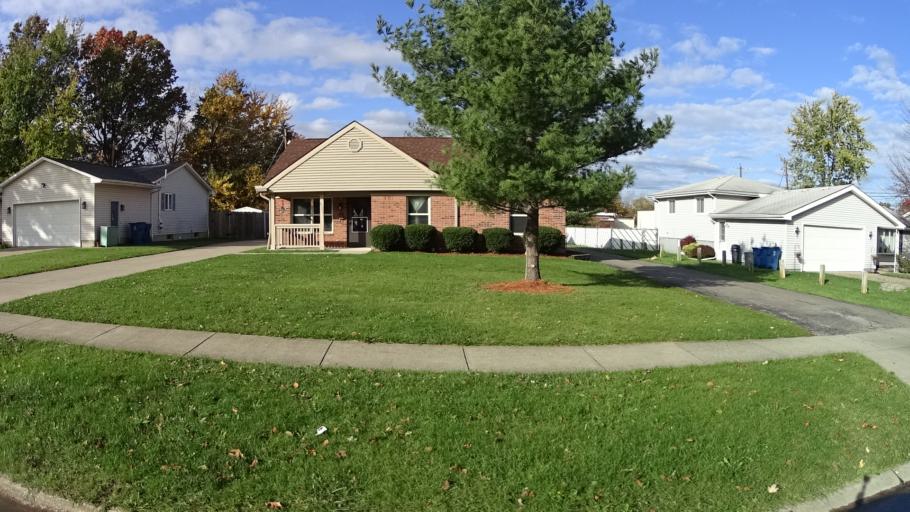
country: US
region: Ohio
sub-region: Lorain County
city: Lorain
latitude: 41.4313
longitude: -82.1835
